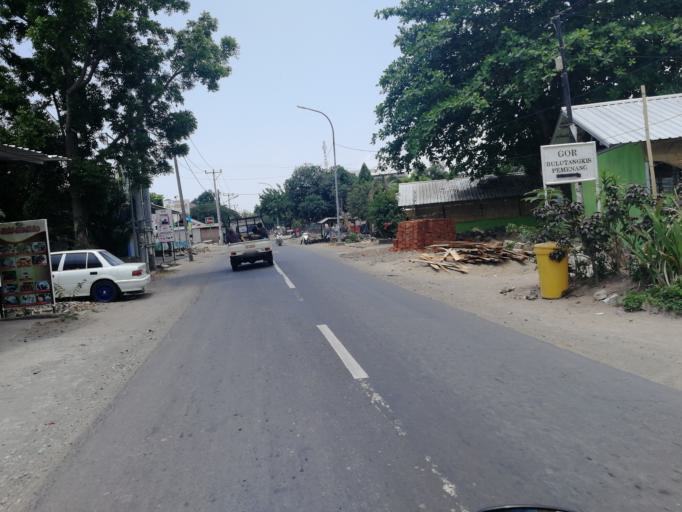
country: ID
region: West Nusa Tenggara
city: Karangsubagan
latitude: -8.4085
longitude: 116.1012
